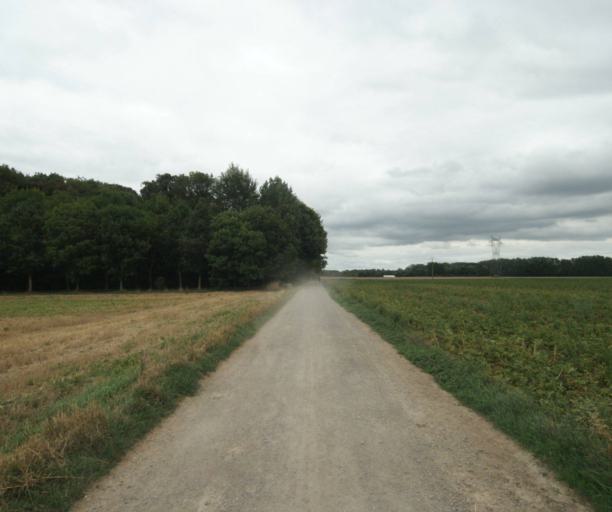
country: FR
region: Nord-Pas-de-Calais
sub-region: Departement du Nord
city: Fretin
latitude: 50.5512
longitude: 3.1304
